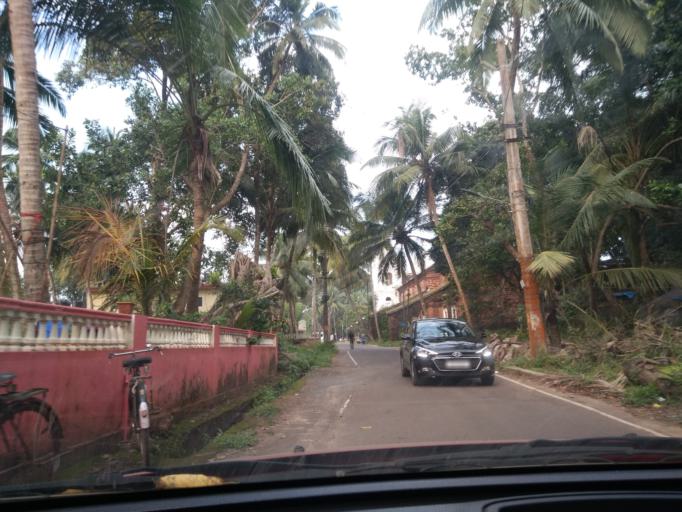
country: IN
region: Goa
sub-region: South Goa
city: Varca
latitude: 15.2318
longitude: 73.9449
